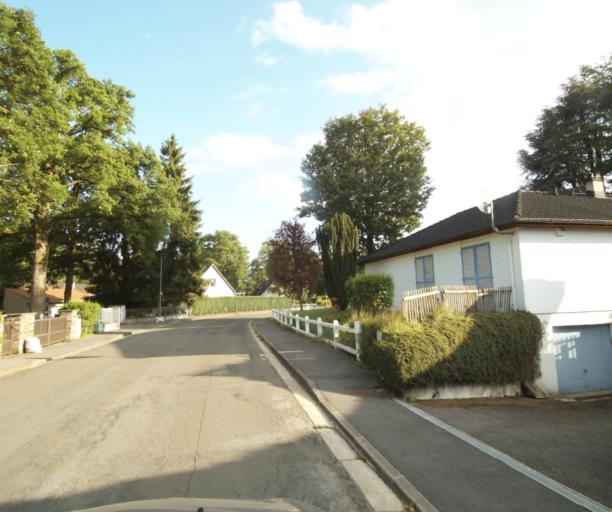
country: FR
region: Champagne-Ardenne
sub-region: Departement des Ardennes
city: Charleville-Mezieres
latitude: 49.7979
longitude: 4.7148
